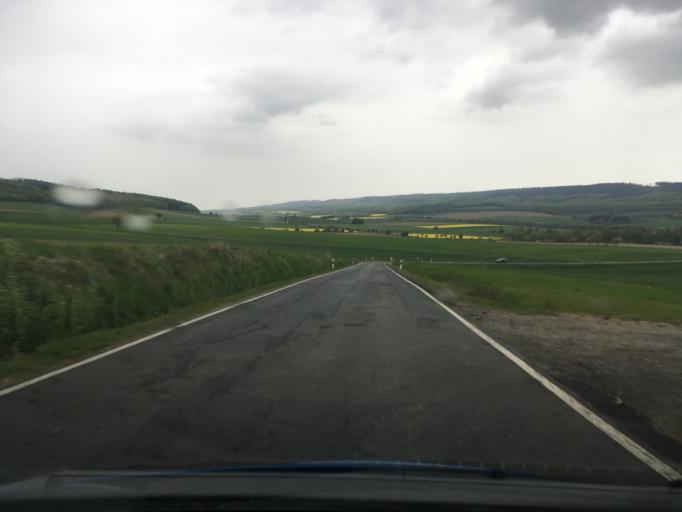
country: DE
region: Lower Saxony
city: Eimen
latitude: 51.8591
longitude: 9.8085
